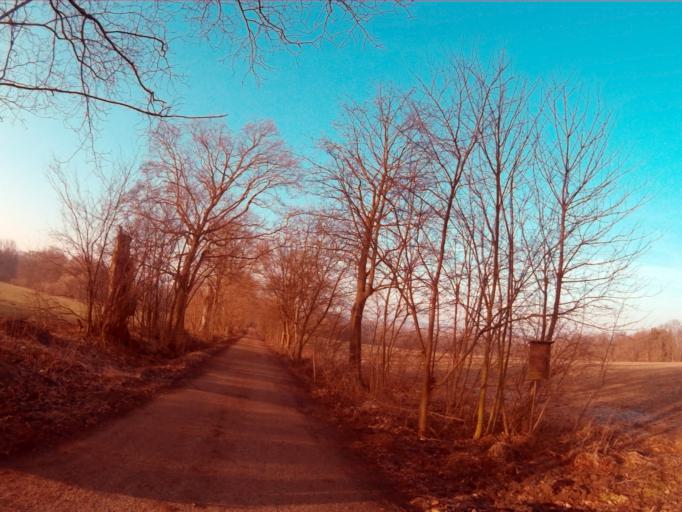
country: CZ
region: Vysocina
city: Namest' nad Oslavou
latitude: 49.1940
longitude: 16.1699
